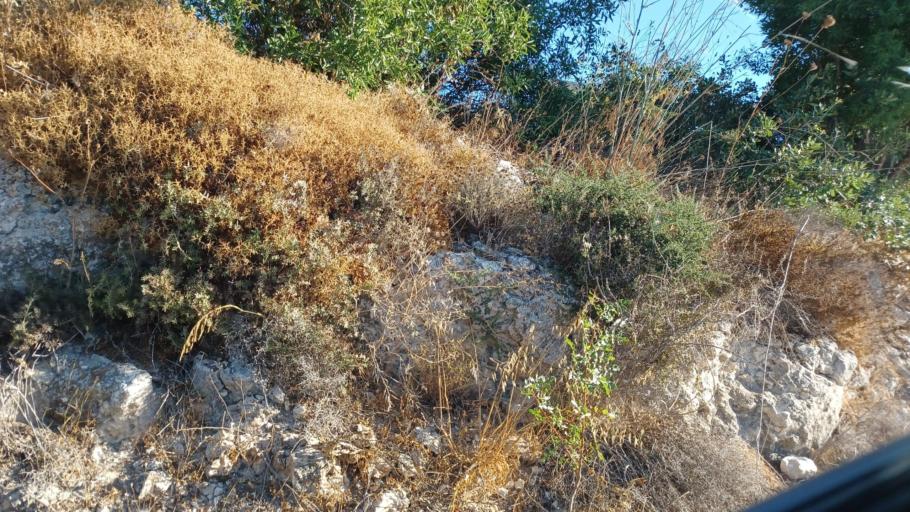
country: CY
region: Pafos
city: Mesogi
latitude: 34.8758
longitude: 32.5032
